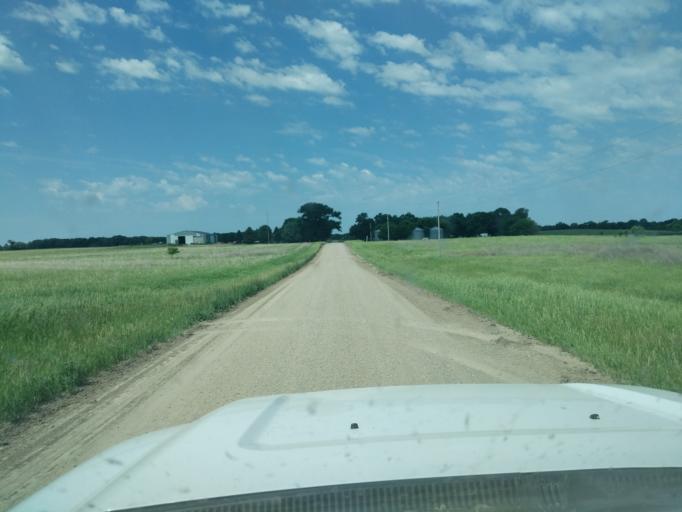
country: US
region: Minnesota
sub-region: Yellow Medicine County
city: Granite Falls
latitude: 44.7453
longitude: -95.3939
